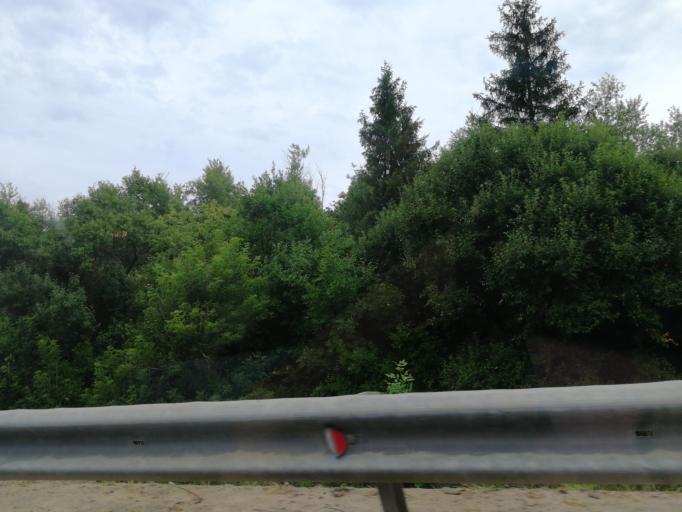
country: RU
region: Tula
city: Bogoroditsk
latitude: 53.7202
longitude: 38.1059
